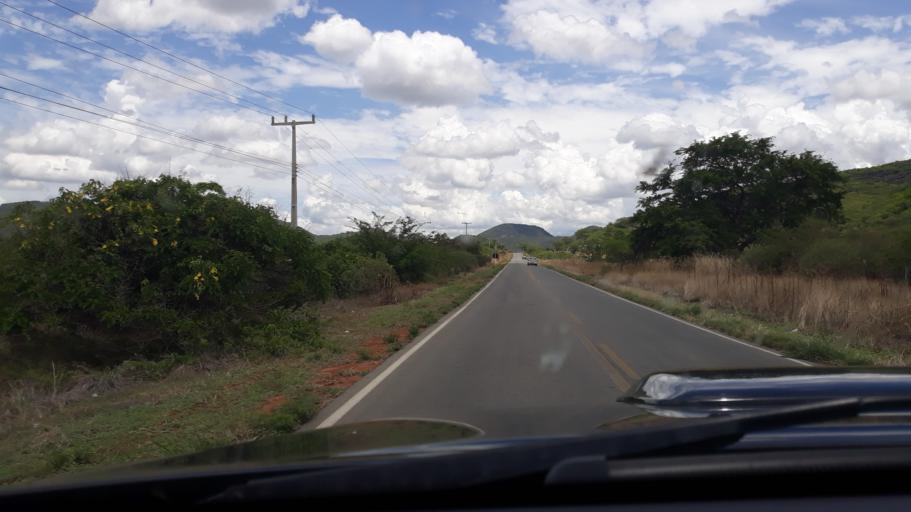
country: BR
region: Bahia
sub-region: Guanambi
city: Guanambi
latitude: -14.2556
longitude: -42.7352
